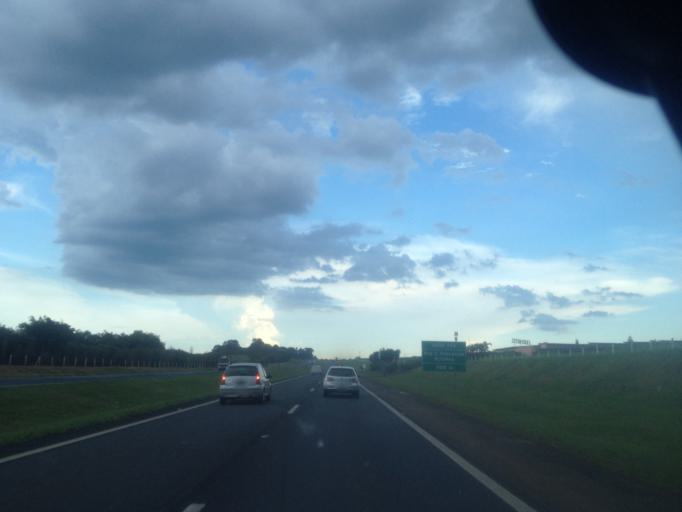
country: BR
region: Sao Paulo
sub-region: Leme
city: Leme
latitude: -22.1396
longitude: -47.4070
